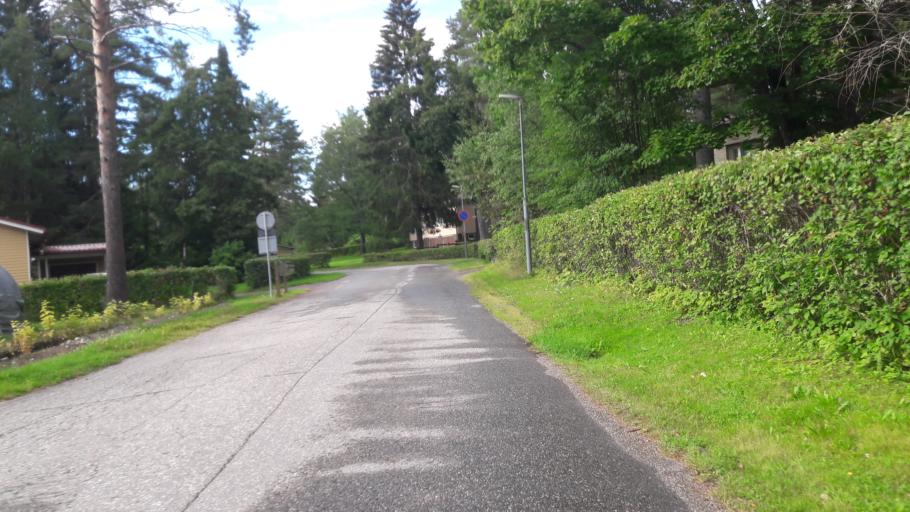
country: FI
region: North Karelia
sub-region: Joensuu
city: Joensuu
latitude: 62.5859
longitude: 29.7856
